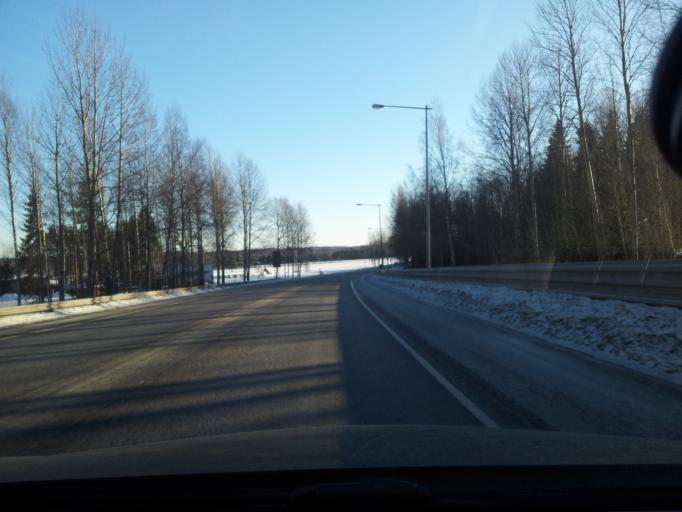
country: FI
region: Uusimaa
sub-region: Helsinki
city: Vihti
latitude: 60.3468
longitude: 24.3319
